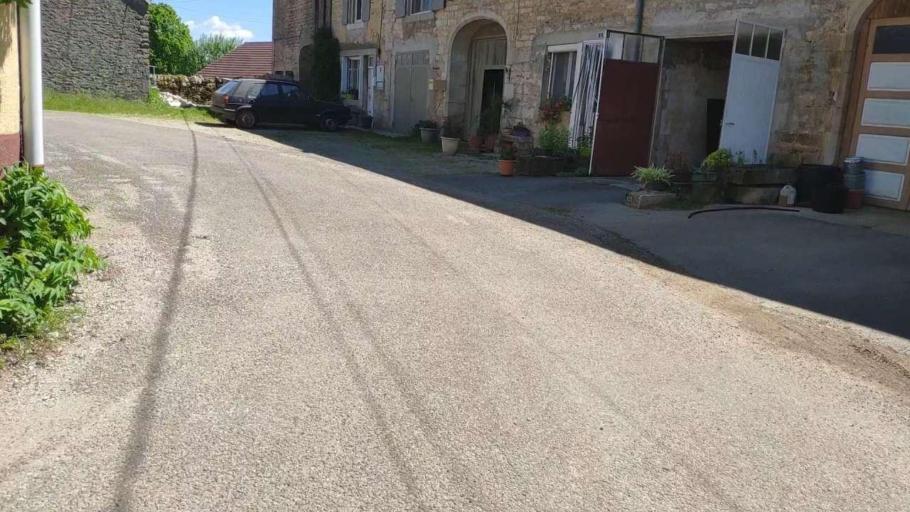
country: FR
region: Franche-Comte
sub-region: Departement du Jura
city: Poligny
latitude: 46.7346
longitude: 5.7006
